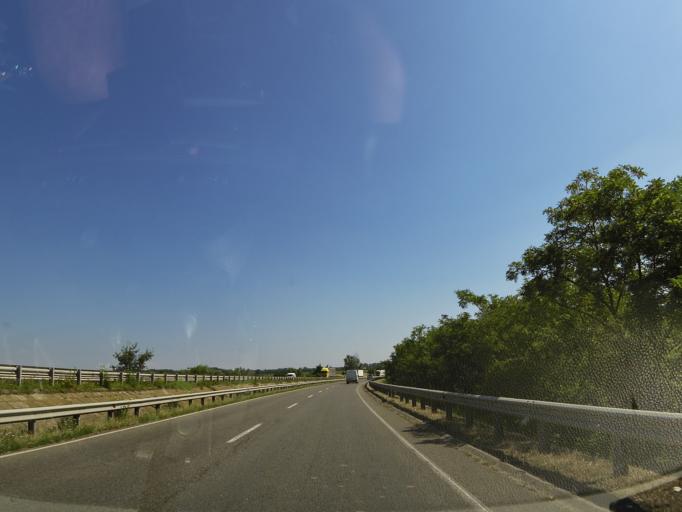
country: HU
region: Jasz-Nagykun-Szolnok
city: Szajol
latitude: 47.1728
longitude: 20.2843
